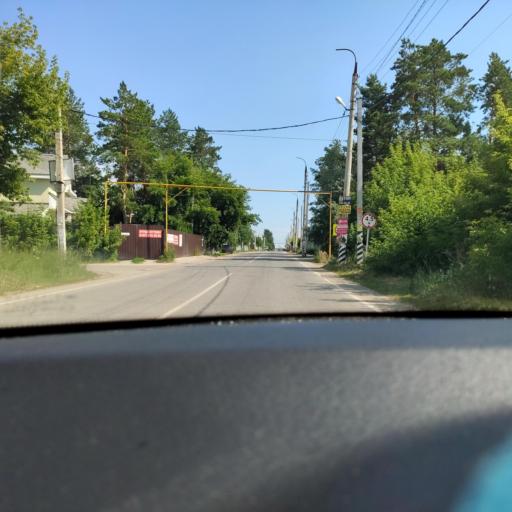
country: RU
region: Samara
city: Volzhskiy
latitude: 53.4521
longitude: 50.1721
